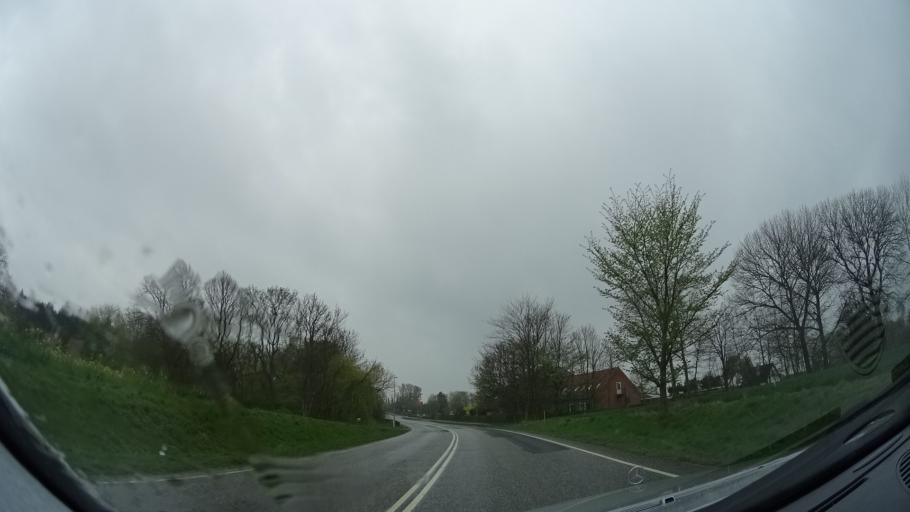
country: DK
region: Zealand
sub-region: Holbaek Kommune
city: Holbaek
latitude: 55.7480
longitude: 11.6195
